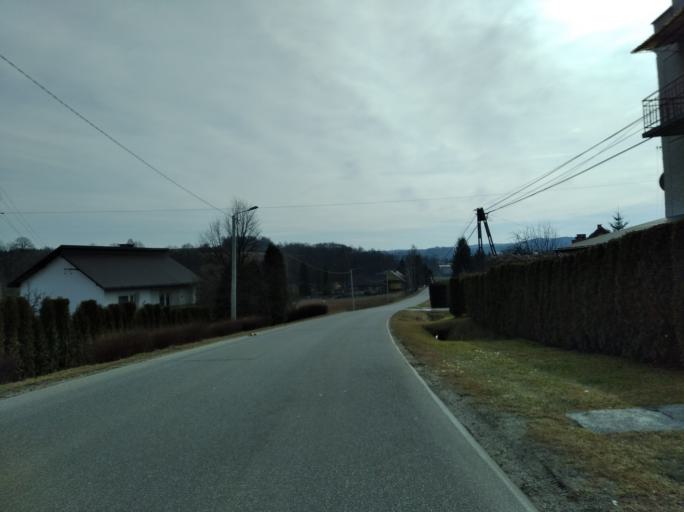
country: PL
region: Subcarpathian Voivodeship
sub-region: Powiat brzozowski
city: Orzechowka
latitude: 49.7360
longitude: 21.9428
